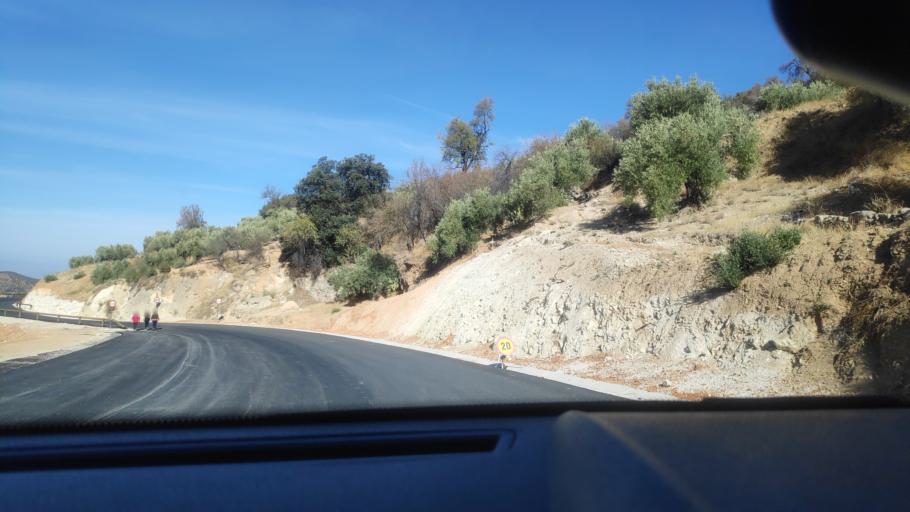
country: ES
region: Andalusia
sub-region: Provincia de Jaen
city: Torres
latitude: 37.7784
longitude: -3.5024
